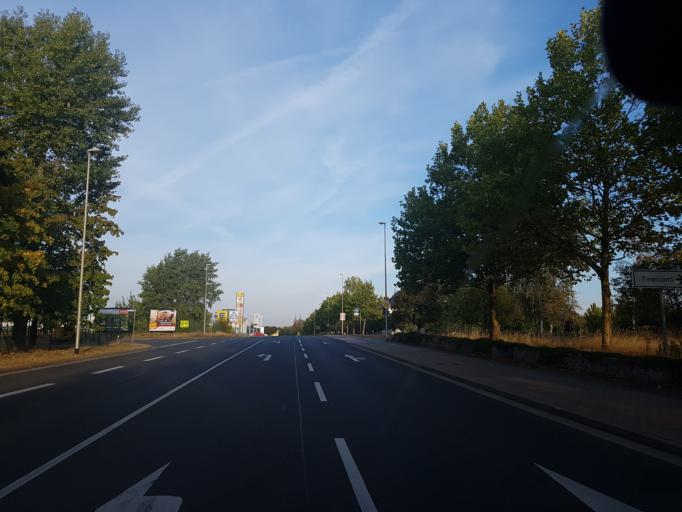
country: DE
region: Saxony
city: Oschatz
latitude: 51.2919
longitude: 13.1278
